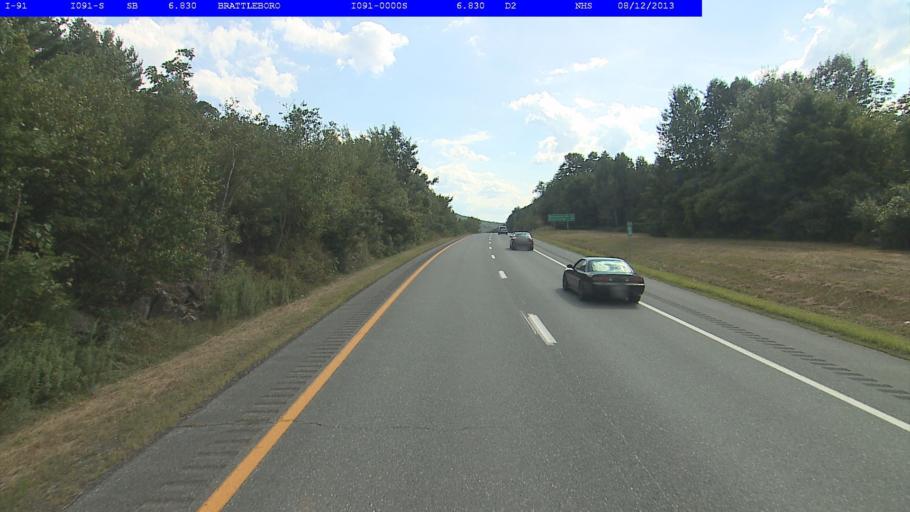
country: US
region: Vermont
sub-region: Windham County
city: Brattleboro
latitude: 42.8264
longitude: -72.5661
